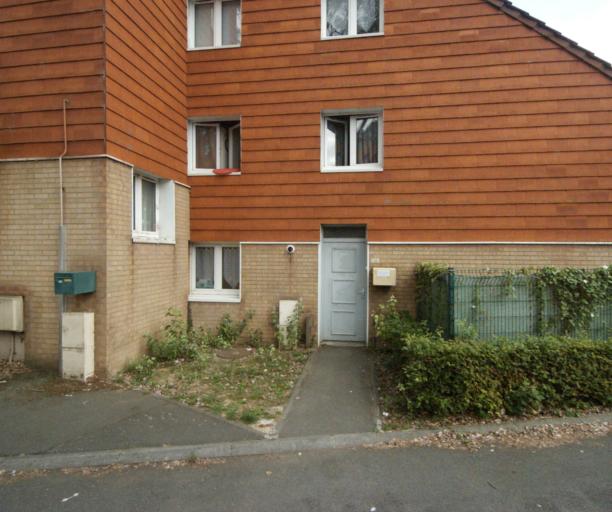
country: FR
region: Nord-Pas-de-Calais
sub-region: Departement du Nord
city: Hem
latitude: 50.6439
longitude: 3.1617
